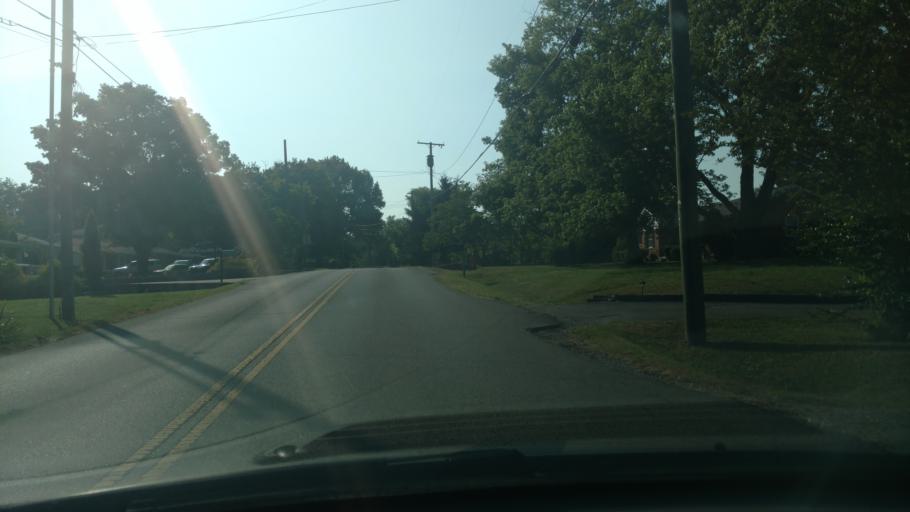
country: US
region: Tennessee
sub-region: Davidson County
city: Nashville
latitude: 36.2214
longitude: -86.7219
